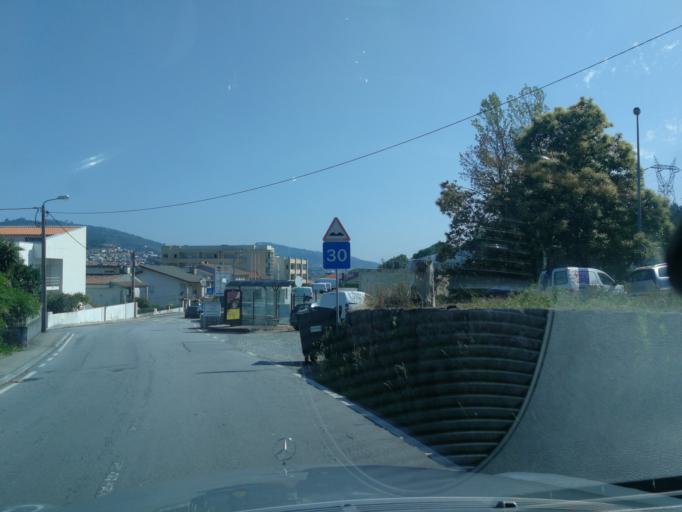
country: PT
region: Braga
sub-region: Braga
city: Adaufe
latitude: 41.5676
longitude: -8.3919
